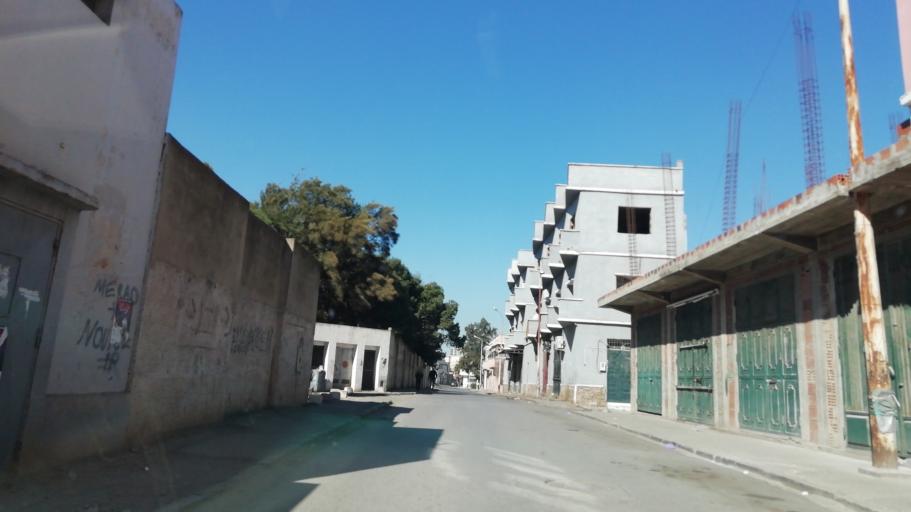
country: DZ
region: Oran
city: Oran
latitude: 35.6916
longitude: -0.6169
